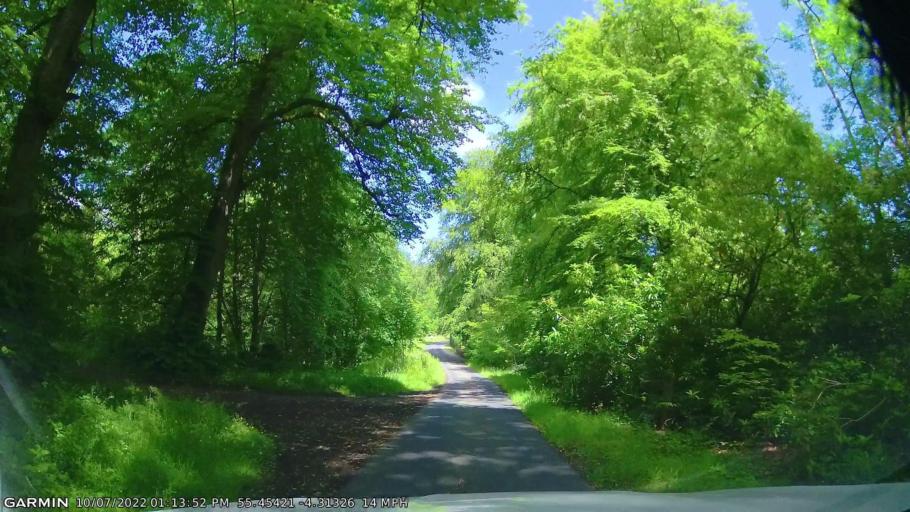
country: GB
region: Scotland
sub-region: East Ayrshire
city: Auchinleck
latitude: 55.4542
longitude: -4.3133
